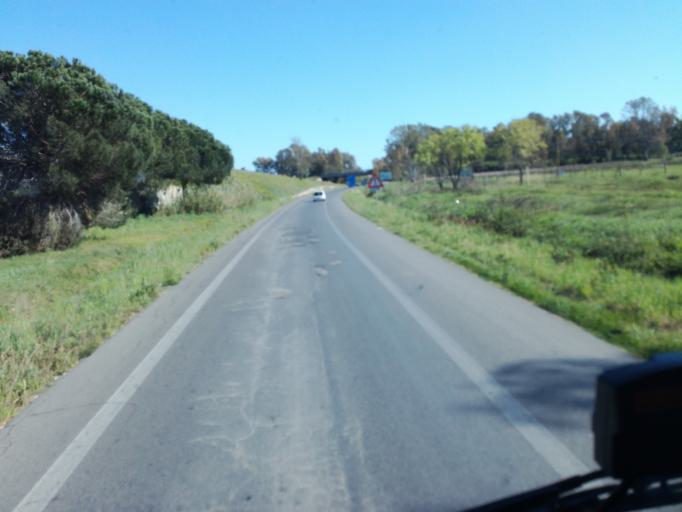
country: IT
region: Latium
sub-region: Provincia di Latina
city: Borgo Podgora
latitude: 41.4832
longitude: 12.8593
